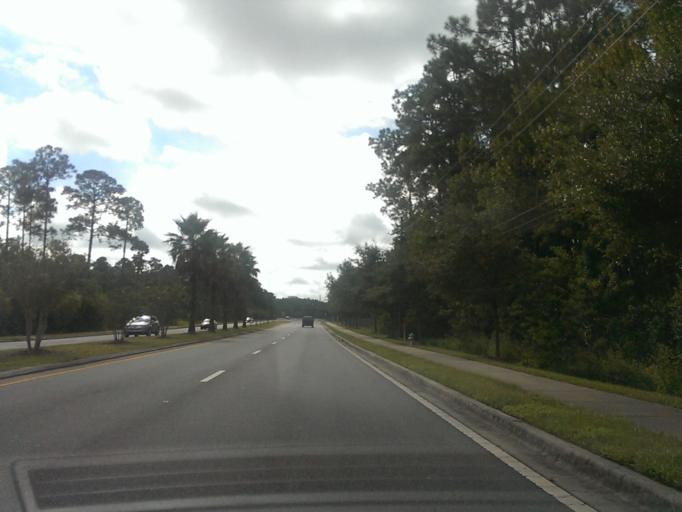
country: US
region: Florida
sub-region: Orange County
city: Doctor Phillips
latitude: 28.3906
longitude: -81.5195
